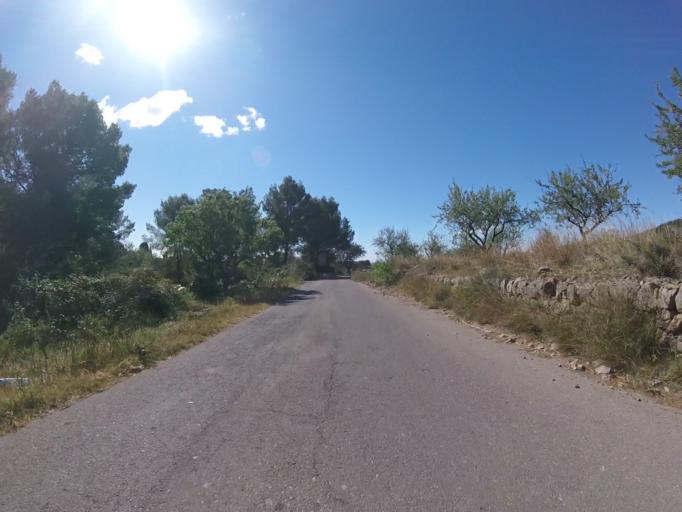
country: ES
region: Valencia
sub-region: Provincia de Castello
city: Benicassim
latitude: 40.0690
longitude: 0.0749
